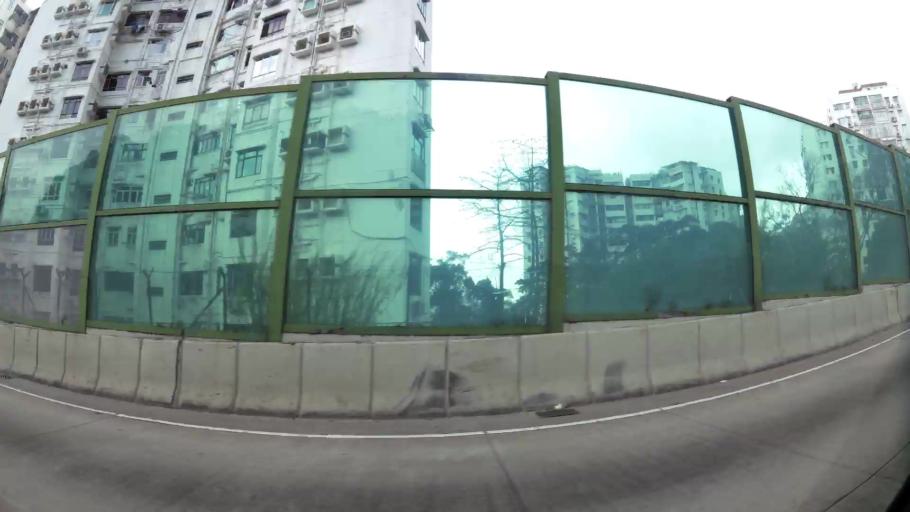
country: HK
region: Wong Tai Sin
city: Wong Tai Sin
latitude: 22.3444
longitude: 114.1782
